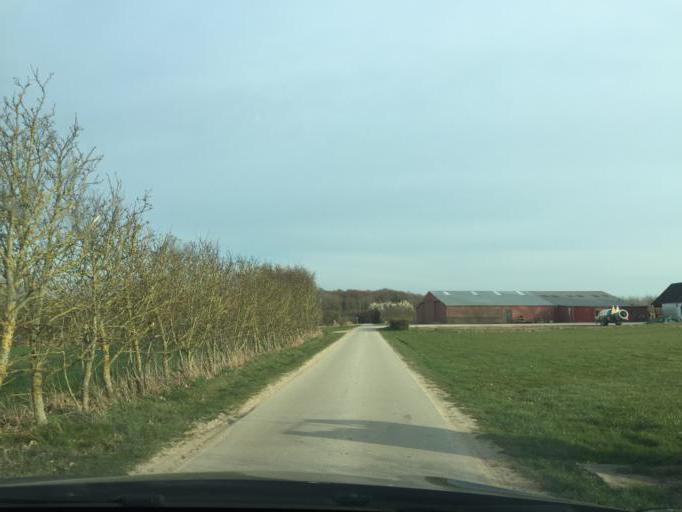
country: DK
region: South Denmark
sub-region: Kerteminde Kommune
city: Langeskov
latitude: 55.3278
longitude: 10.5843
